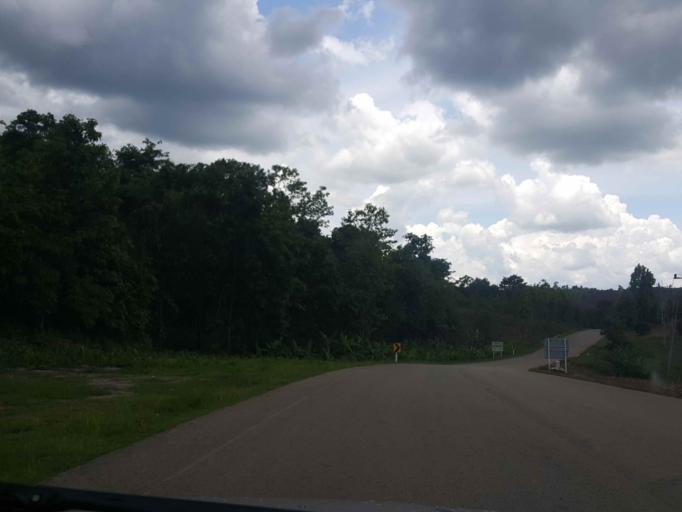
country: TH
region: Phayao
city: Dok Kham Tai
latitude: 18.9726
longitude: 100.0739
